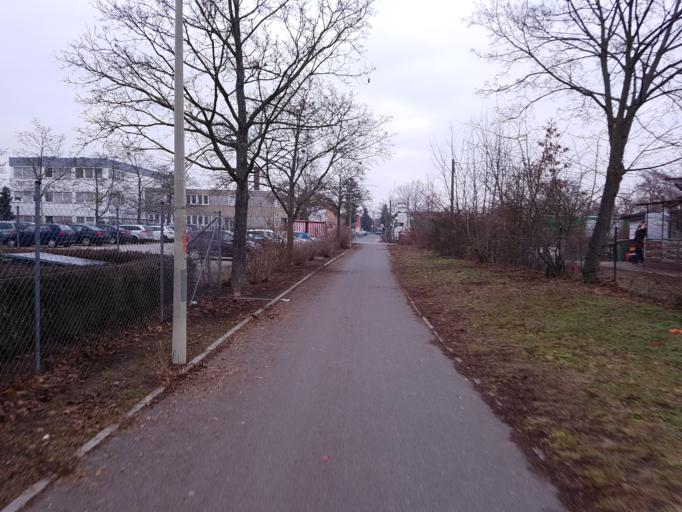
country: DE
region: Bavaria
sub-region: Regierungsbezirk Mittelfranken
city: Grossreuth bei Schweinau
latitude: 49.4475
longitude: 11.0322
